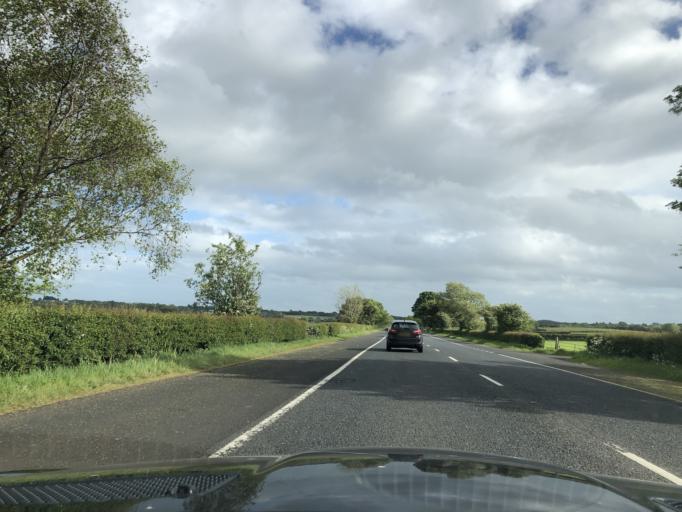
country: GB
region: Northern Ireland
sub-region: Ballymoney District
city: Ballymoney
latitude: 55.0956
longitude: -6.5346
